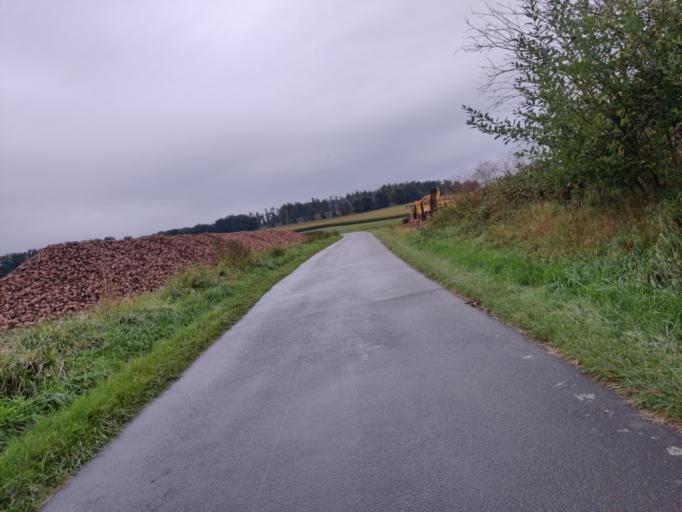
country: DE
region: Lower Saxony
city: Furstenberg
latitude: 51.7307
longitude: 9.3873
